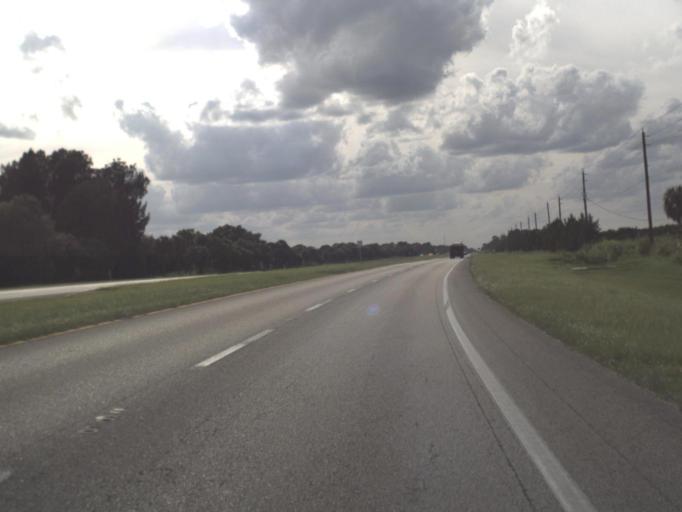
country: US
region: Florida
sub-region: Hendry County
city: LaBelle
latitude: 26.7103
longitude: -81.5107
